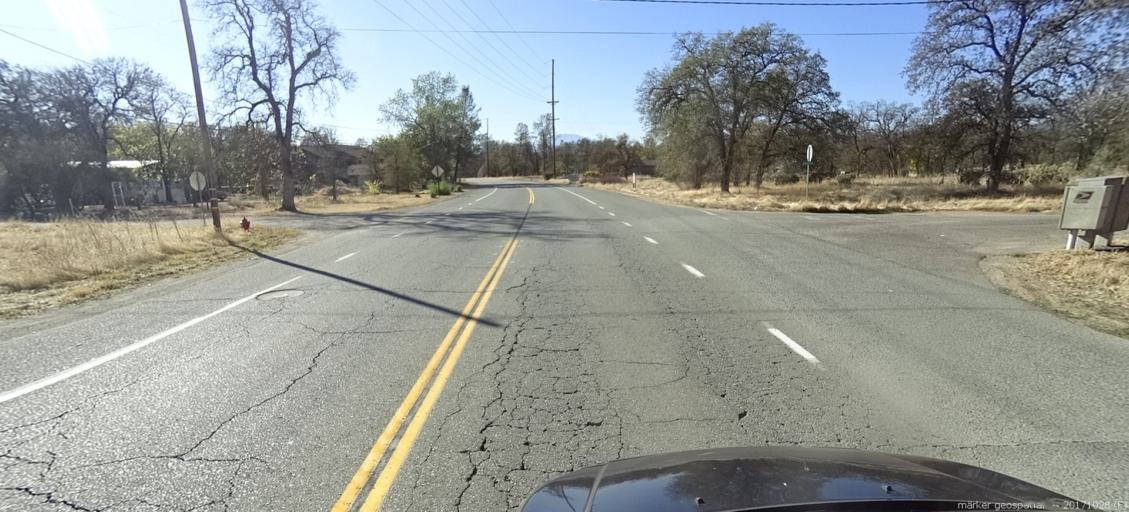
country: US
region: California
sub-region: Shasta County
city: Central Valley (historical)
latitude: 40.6421
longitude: -122.3712
